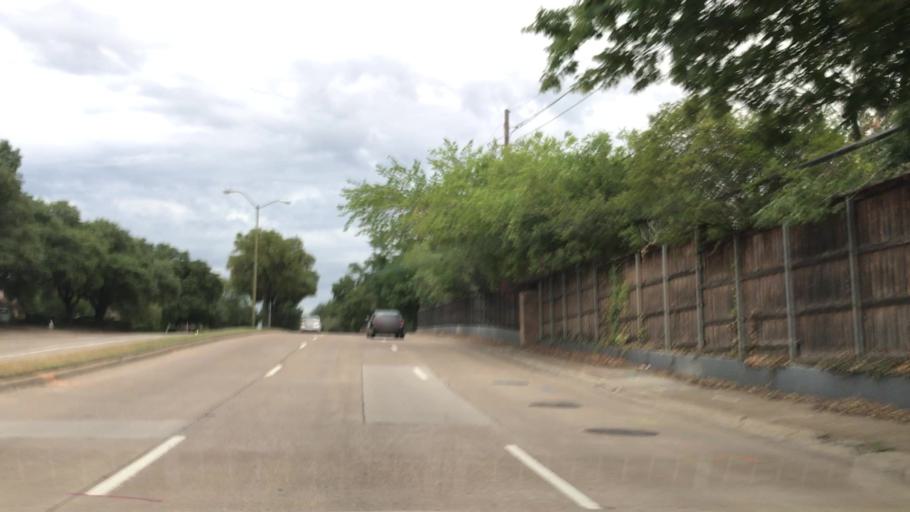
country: US
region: Texas
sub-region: Dallas County
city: University Park
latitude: 32.9013
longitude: -96.7884
